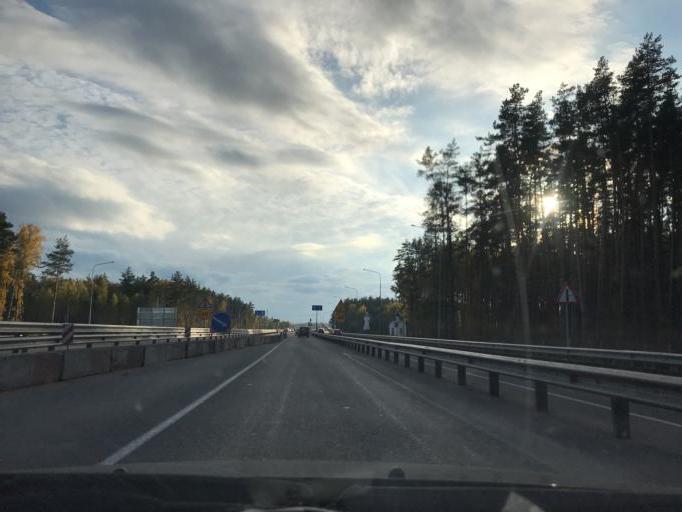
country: RU
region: Kaluga
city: Kurovskoye
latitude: 54.5680
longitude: 36.0519
